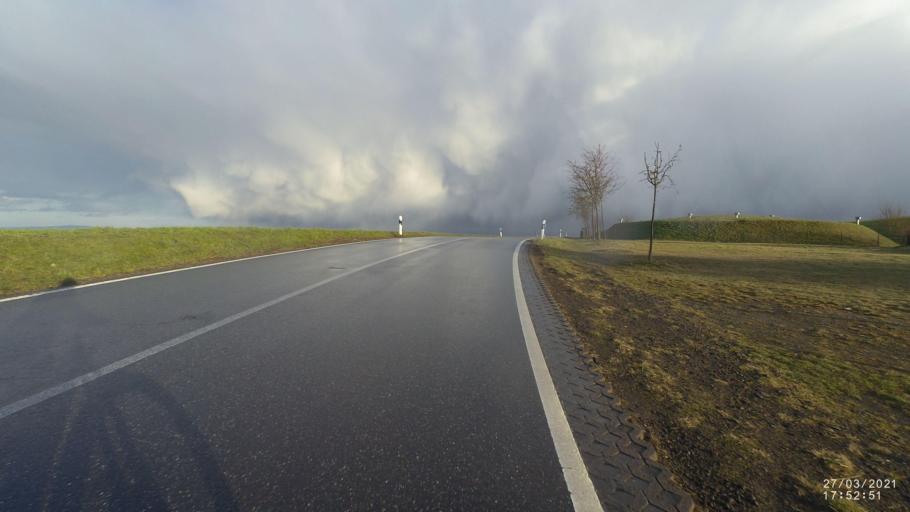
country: DE
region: Rheinland-Pfalz
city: Bell
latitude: 50.3837
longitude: 7.2439
